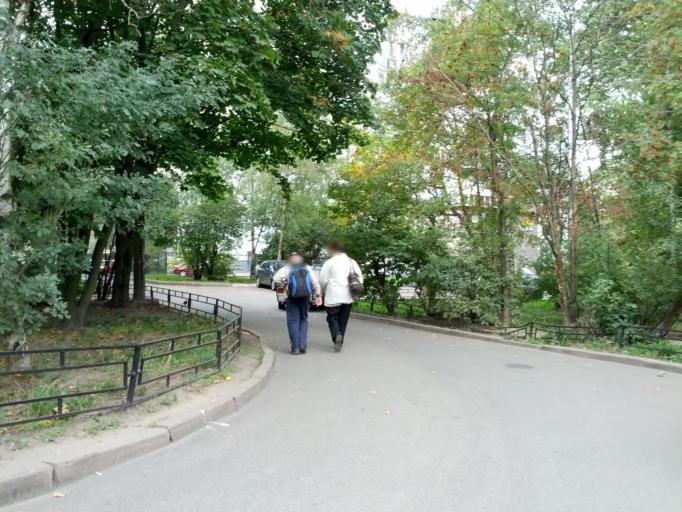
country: RU
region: Leningrad
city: Rybatskoye
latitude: 59.9026
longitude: 30.4854
